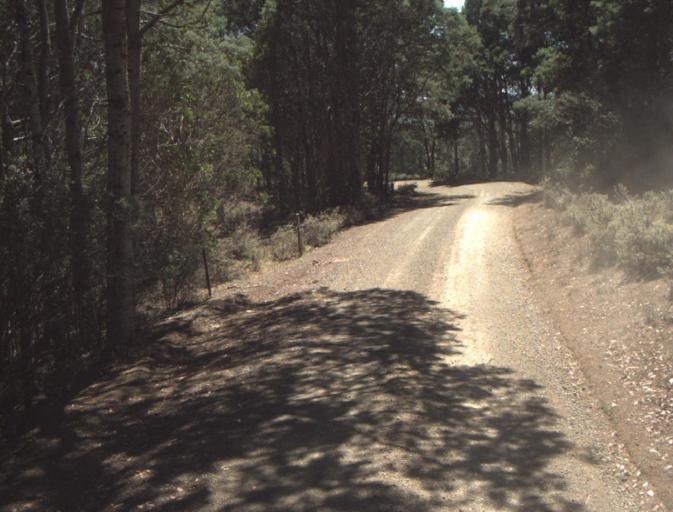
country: AU
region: Tasmania
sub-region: Dorset
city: Scottsdale
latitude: -41.3548
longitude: 147.4253
